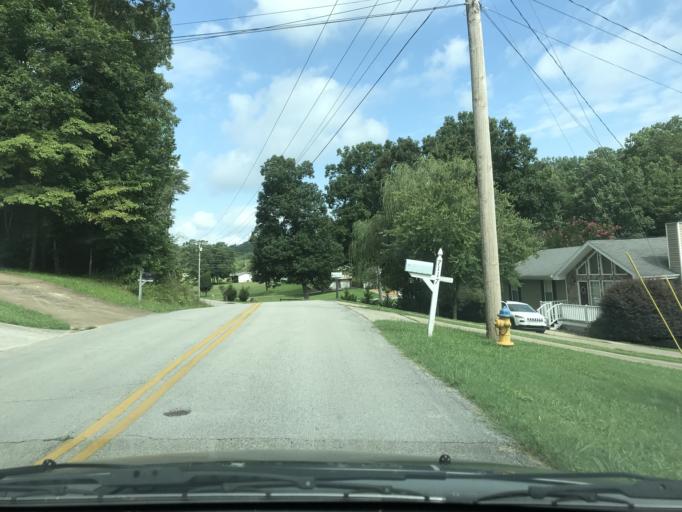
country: US
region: Tennessee
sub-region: Hamilton County
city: Lakesite
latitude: 35.1807
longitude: -85.0700
